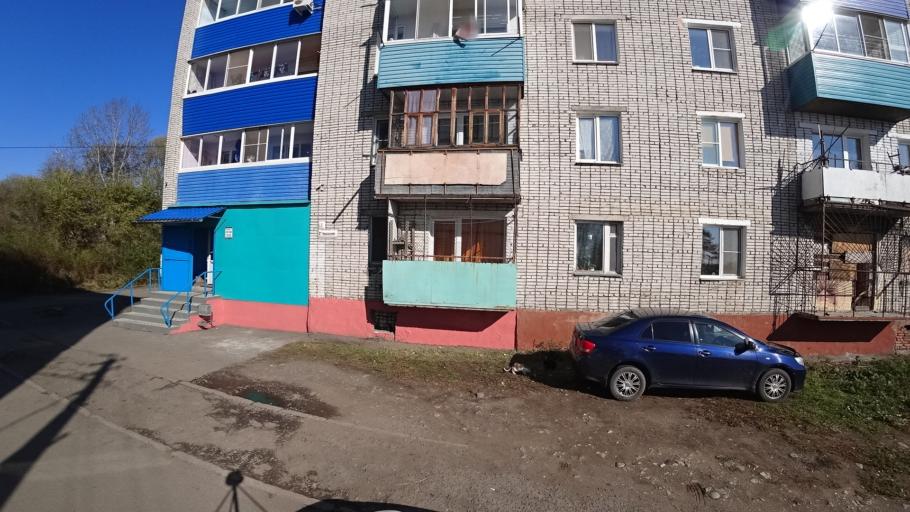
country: RU
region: Khabarovsk Krai
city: Amursk
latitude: 50.0973
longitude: 136.5156
